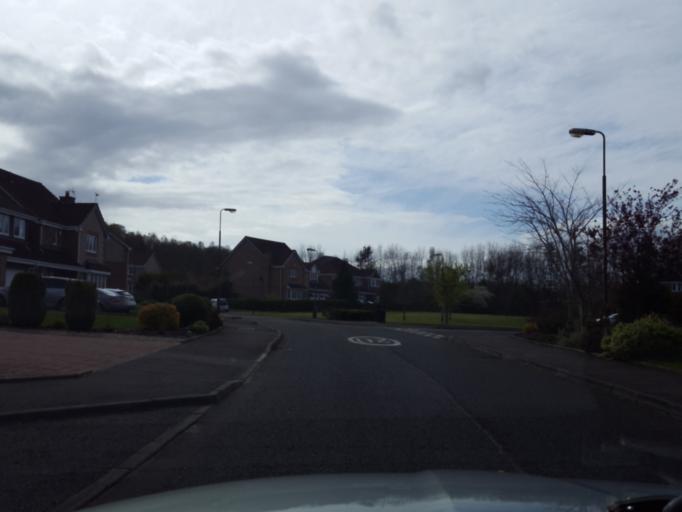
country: GB
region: Scotland
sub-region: West Lothian
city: Linlithgow
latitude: 55.9685
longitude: -3.6215
